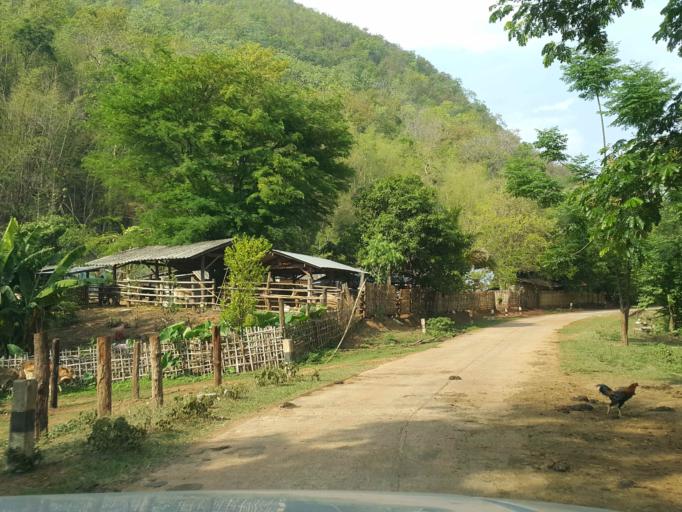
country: TH
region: Chiang Mai
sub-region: Amphoe Chiang Dao
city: Chiang Dao
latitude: 19.4003
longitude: 98.7751
